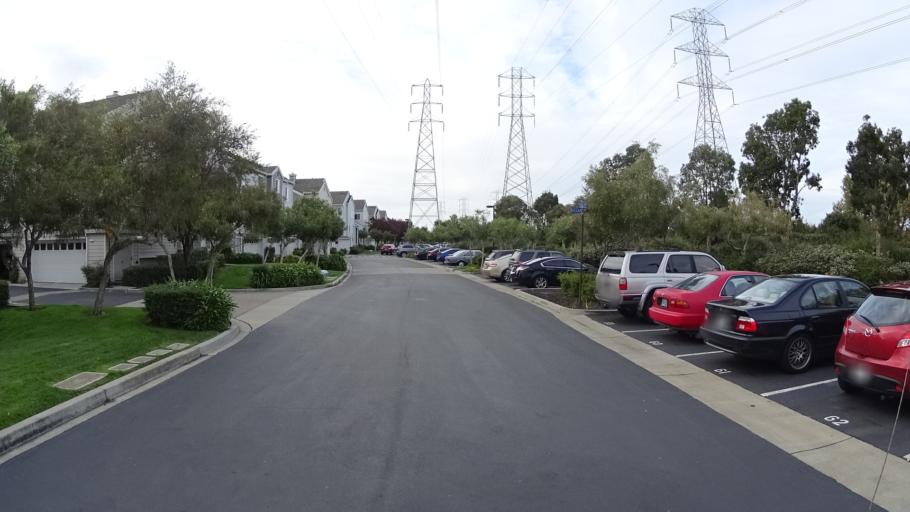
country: US
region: California
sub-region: San Mateo County
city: Redwood Shores
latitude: 37.5428
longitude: -122.2373
